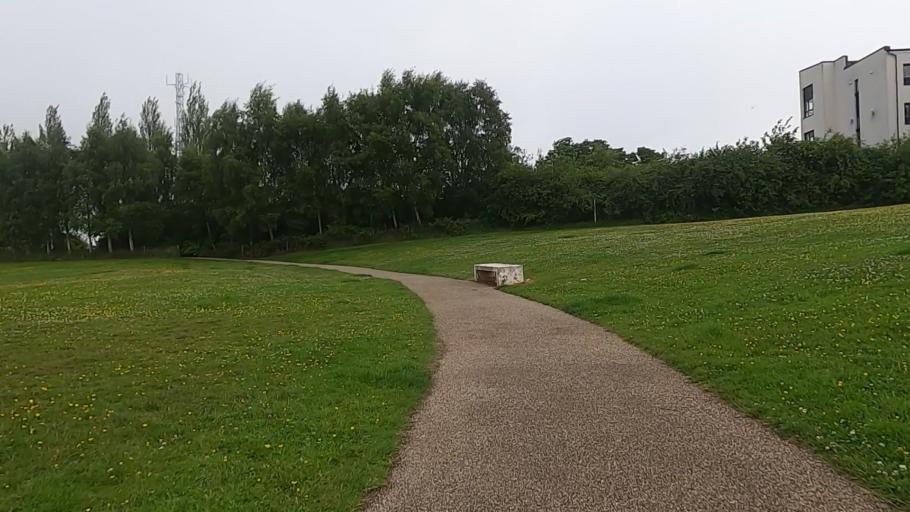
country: GB
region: Scotland
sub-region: Edinburgh
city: Edinburgh
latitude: 55.9780
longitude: -3.2493
